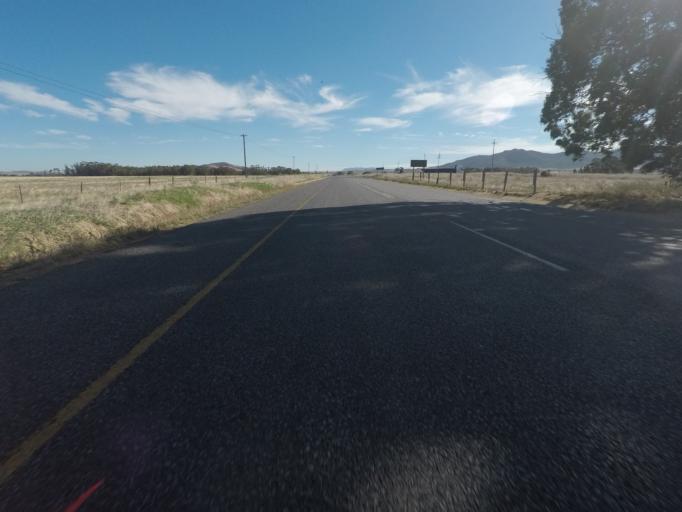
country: ZA
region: Western Cape
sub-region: West Coast District Municipality
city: Malmesbury
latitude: -33.6228
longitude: 18.7252
